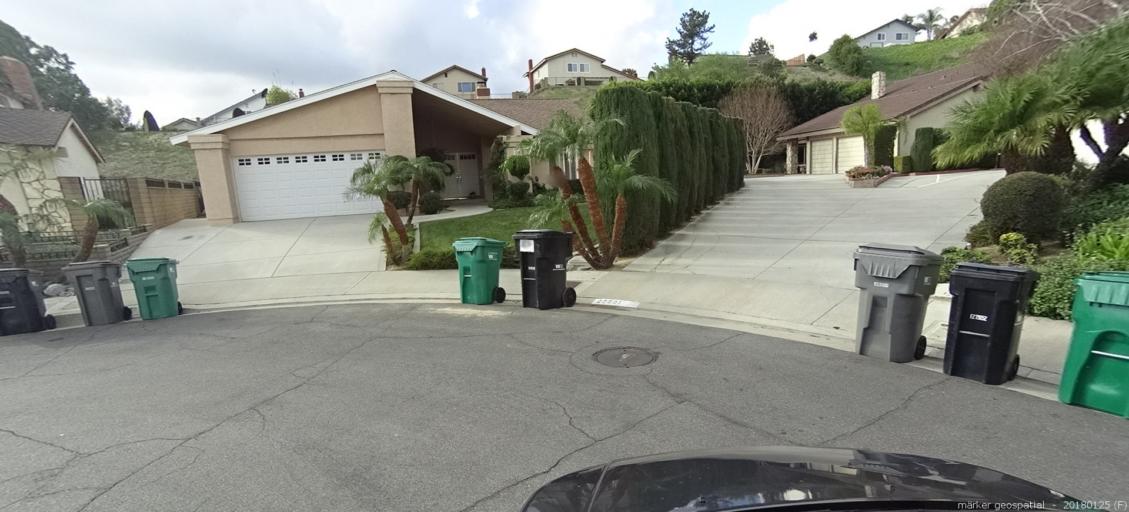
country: US
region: California
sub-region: Los Angeles County
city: Diamond Bar
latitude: 33.9968
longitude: -117.8210
